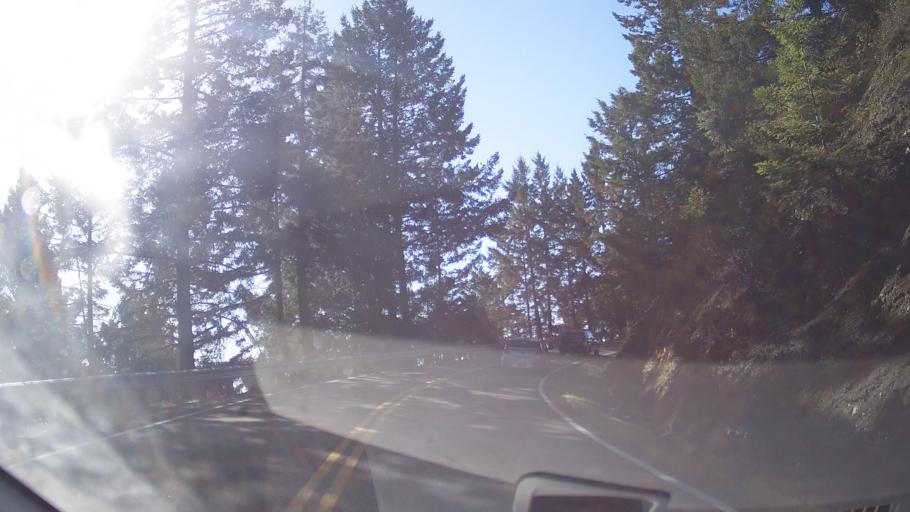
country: US
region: California
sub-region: Marin County
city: Mill Valley
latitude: 37.9114
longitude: -122.5970
